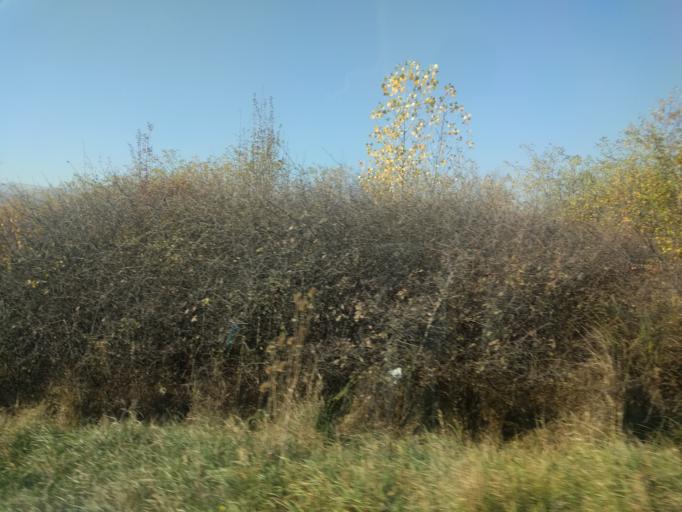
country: XK
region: Pristina
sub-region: Komuna e Gracanices
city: Glanica
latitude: 42.5890
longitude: 21.0174
